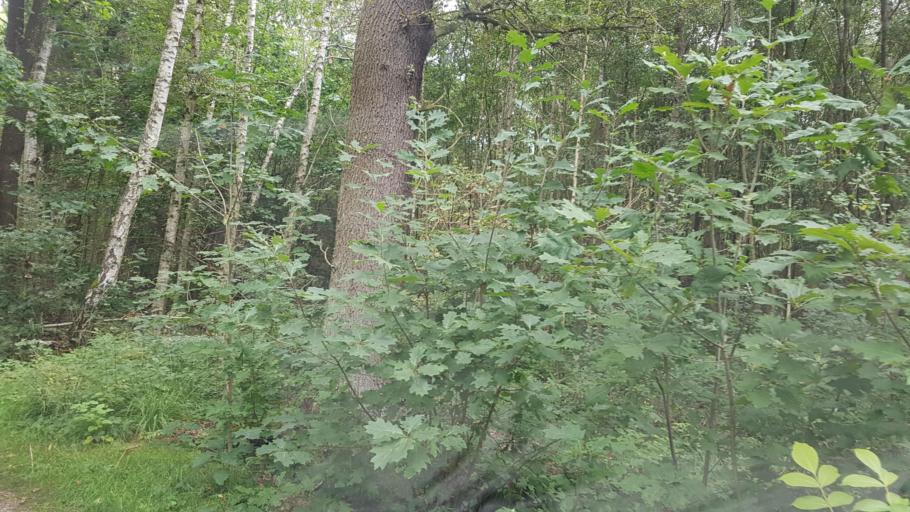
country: DE
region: Brandenburg
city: Doberlug-Kirchhain
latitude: 51.6387
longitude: 13.5293
